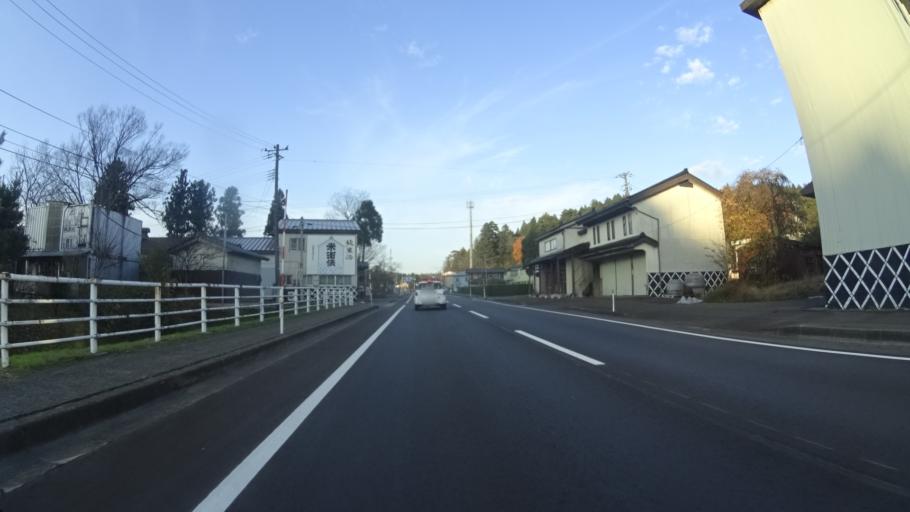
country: JP
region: Niigata
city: Nagaoka
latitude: 37.4313
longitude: 138.7276
